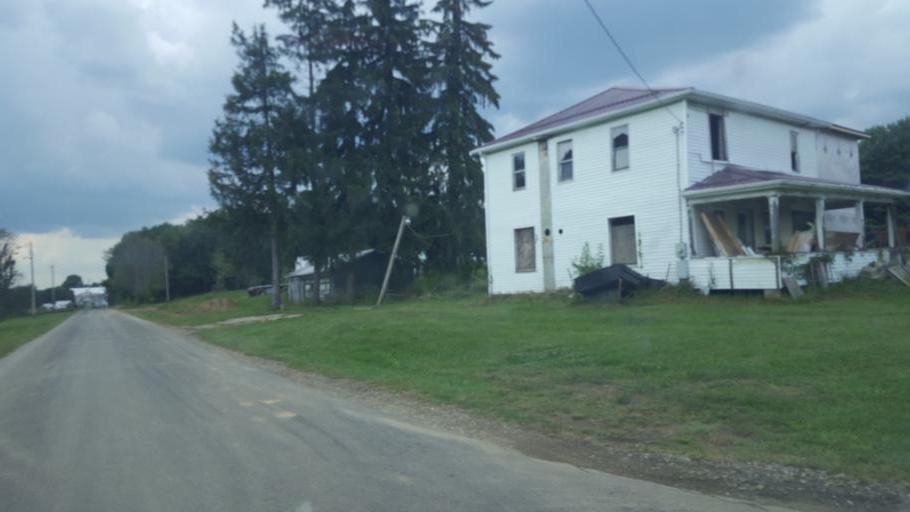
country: US
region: Ohio
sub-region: Knox County
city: Oak Hill
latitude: 40.3557
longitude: -82.2994
